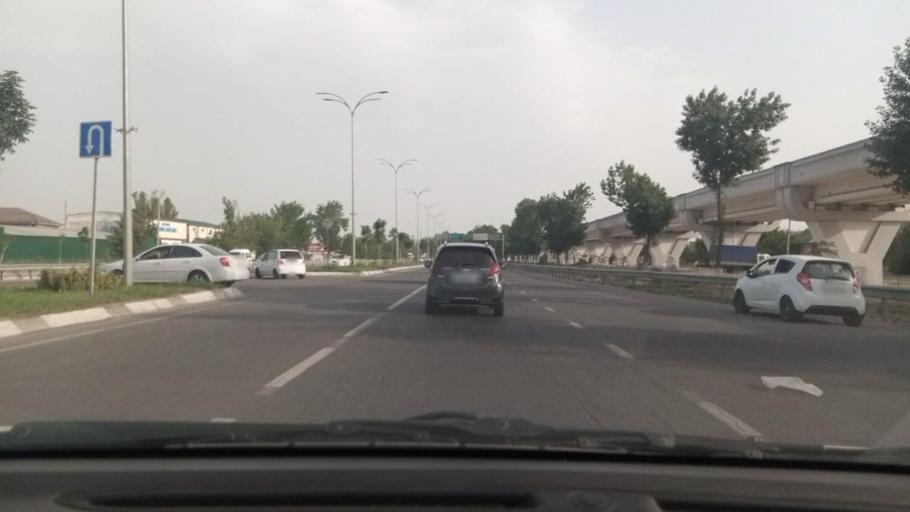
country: UZ
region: Toshkent Shahri
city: Bektemir
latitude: 41.2756
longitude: 69.3617
